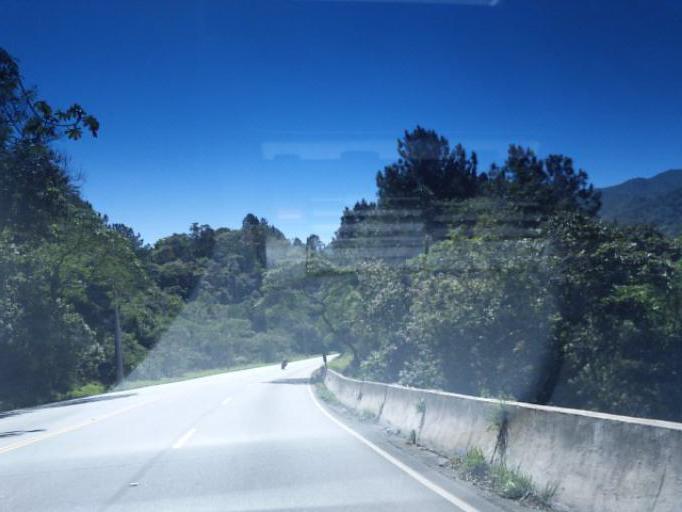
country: BR
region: Sao Paulo
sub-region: Campos Do Jordao
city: Campos do Jordao
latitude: -22.8266
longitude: -45.6270
